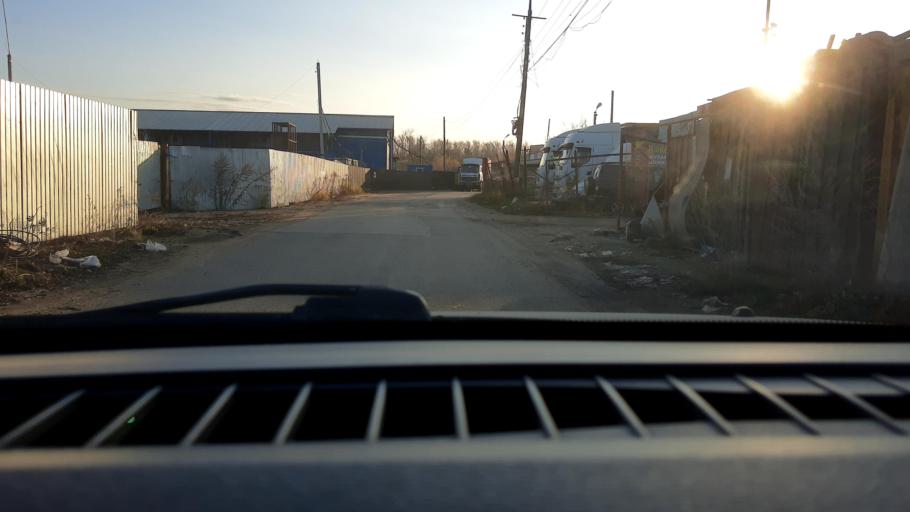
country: RU
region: Nizjnij Novgorod
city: Gorbatovka
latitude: 56.3176
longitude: 43.8568
